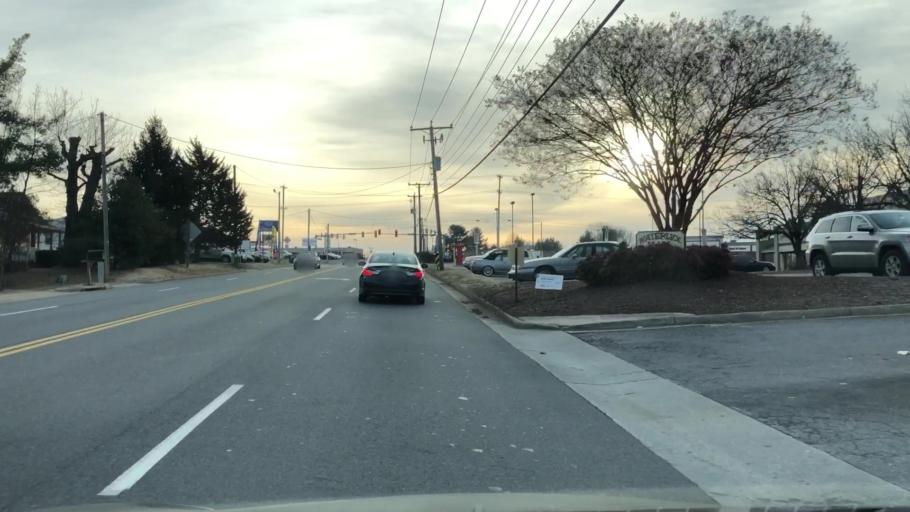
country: US
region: Virginia
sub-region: Campbell County
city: Timberlake
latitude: 37.3298
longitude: -79.2485
